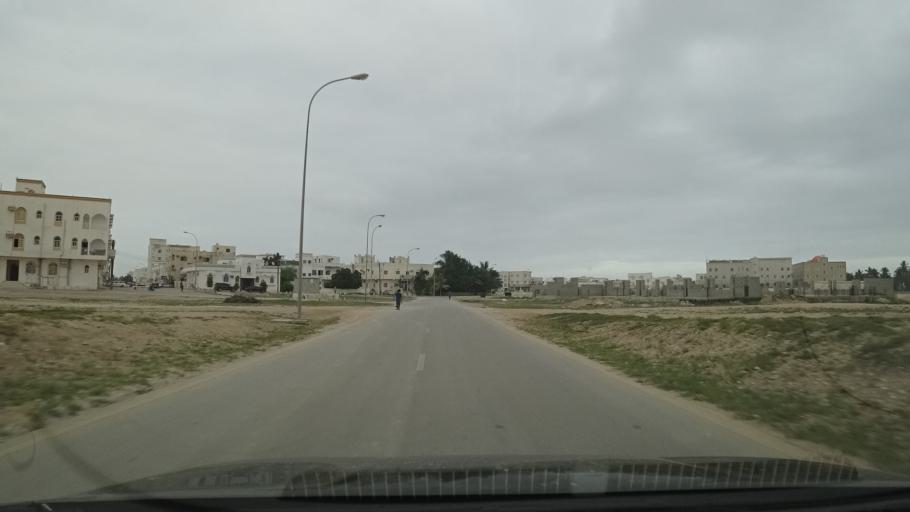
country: OM
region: Zufar
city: Salalah
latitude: 17.0238
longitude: 54.1546
